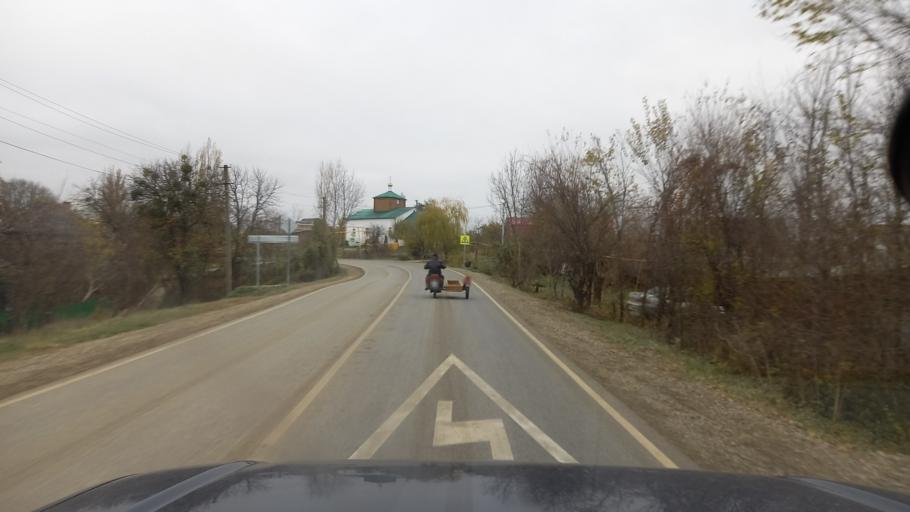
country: RU
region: Krasnodarskiy
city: Goryachiy Klyuch
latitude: 44.5200
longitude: 39.2921
